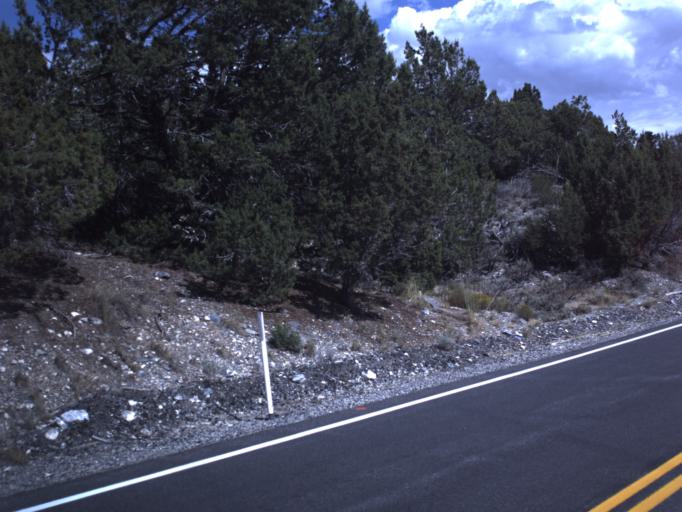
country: US
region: Utah
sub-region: Tooele County
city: Grantsville
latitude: 40.3490
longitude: -112.5572
